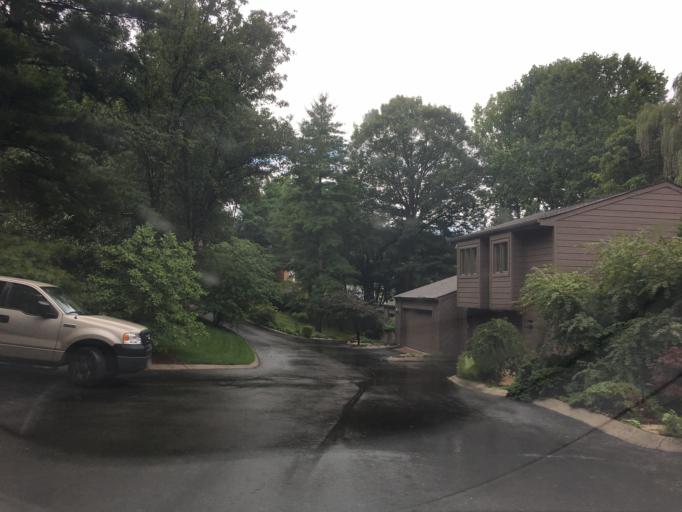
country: US
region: Tennessee
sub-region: Davidson County
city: Belle Meade
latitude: 36.0742
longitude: -86.8973
